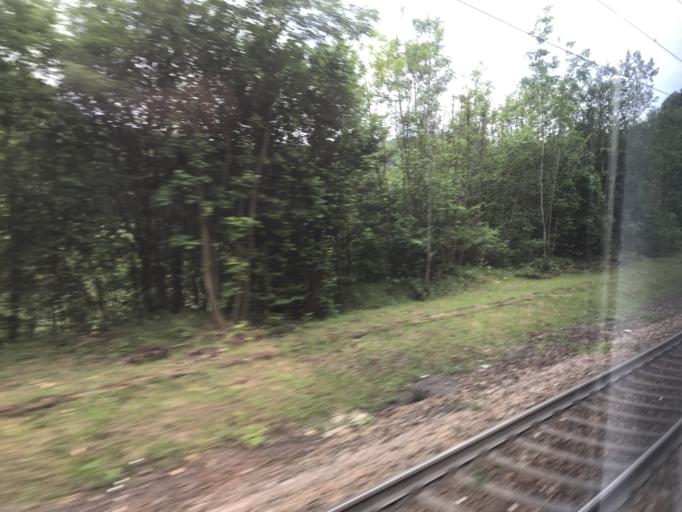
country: DE
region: Baden-Wuerttemberg
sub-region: Tuebingen Region
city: Amstetten
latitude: 48.5970
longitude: 9.8517
